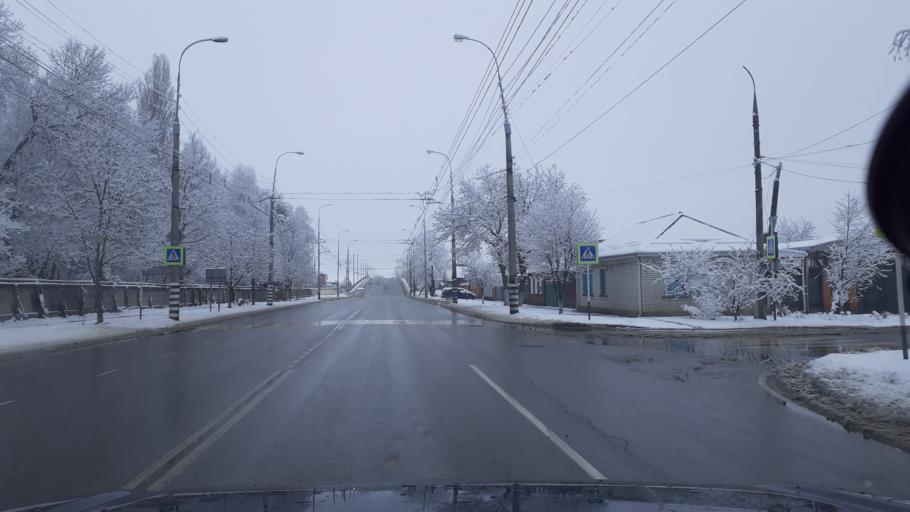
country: RU
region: Adygeya
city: Maykop
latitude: 44.6175
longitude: 40.1210
